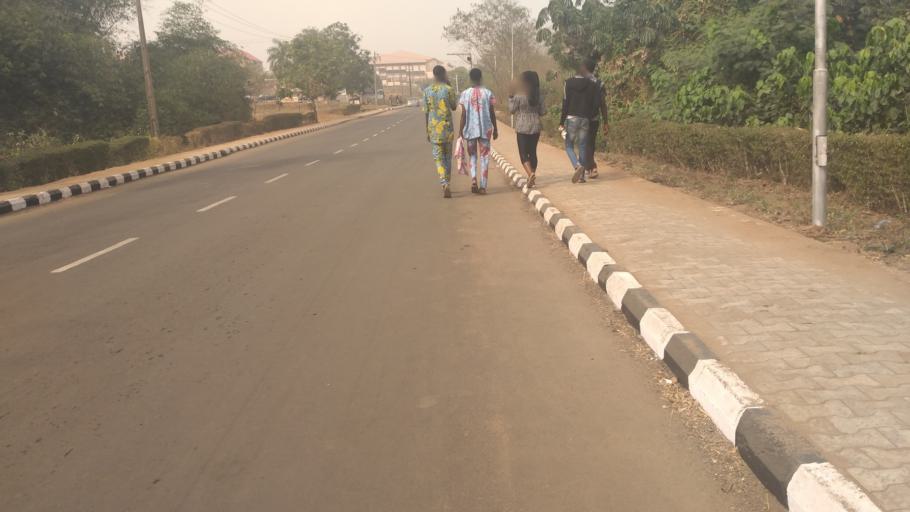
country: NG
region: Ondo
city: Ilare
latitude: 7.3001
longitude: 5.1358
